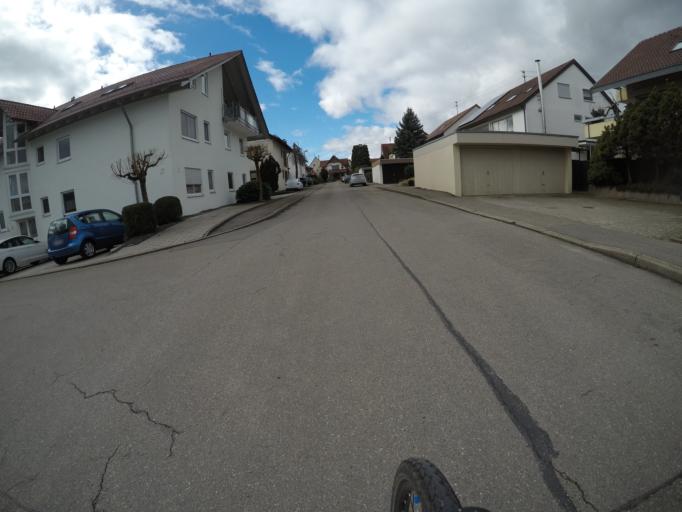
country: DE
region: Baden-Wuerttemberg
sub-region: Regierungsbezirk Stuttgart
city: Ehningen
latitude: 48.6630
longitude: 8.9475
